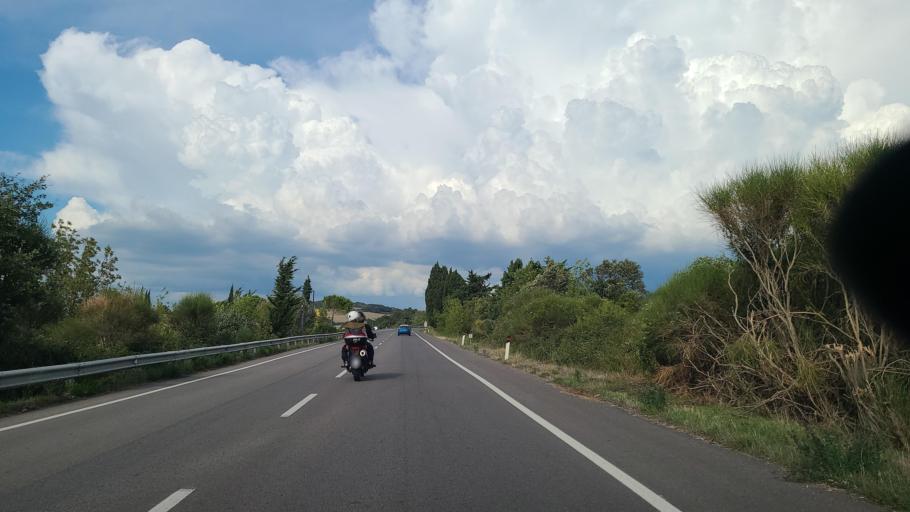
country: IT
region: Tuscany
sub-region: Province of Pisa
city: Volterra
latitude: 43.3979
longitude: 10.9622
